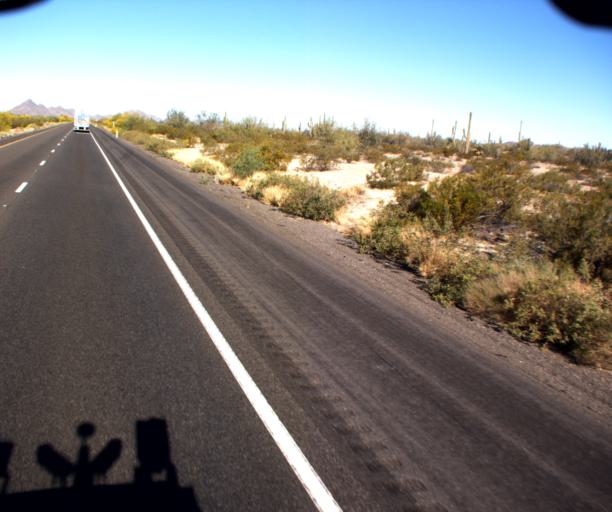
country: US
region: Arizona
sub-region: Maricopa County
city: Gila Bend
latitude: 32.8699
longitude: -112.4310
